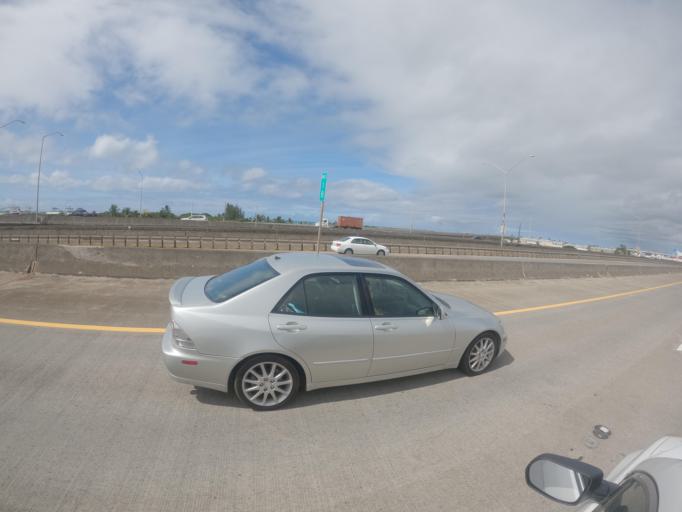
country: US
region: Hawaii
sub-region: Honolulu County
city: Honolulu
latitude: 21.3347
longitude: -157.8951
